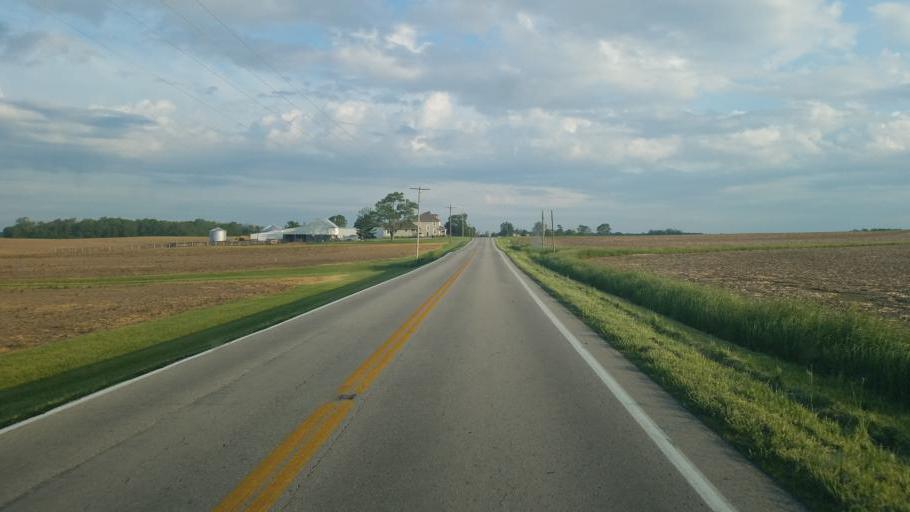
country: US
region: Ohio
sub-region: Highland County
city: Leesburg
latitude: 39.4034
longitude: -83.6026
